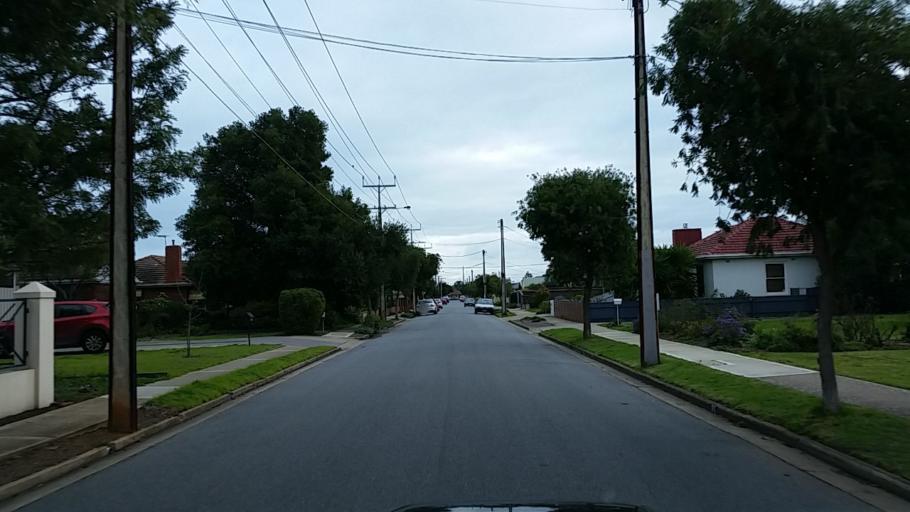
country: AU
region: South Australia
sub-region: Marion
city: South Plympton
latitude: -34.9794
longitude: 138.5597
